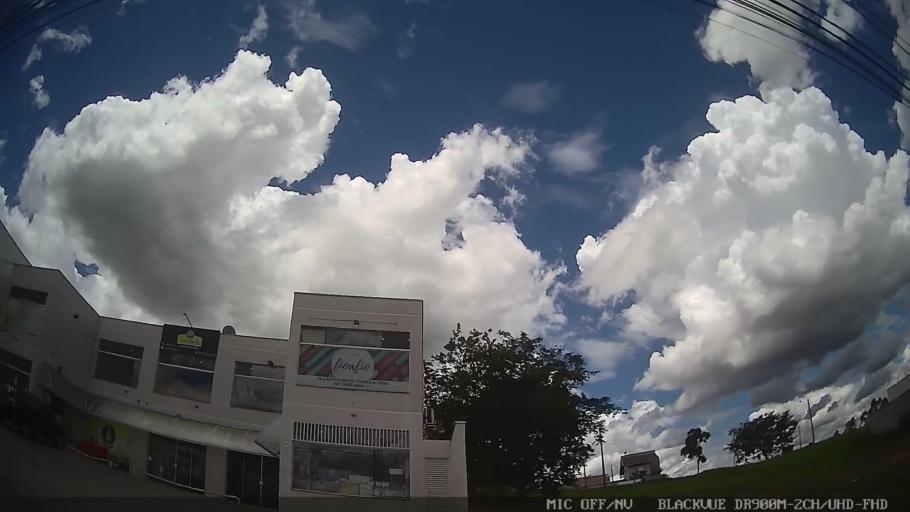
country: BR
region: Sao Paulo
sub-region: Jaguariuna
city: Jaguariuna
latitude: -22.6880
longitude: -46.9899
